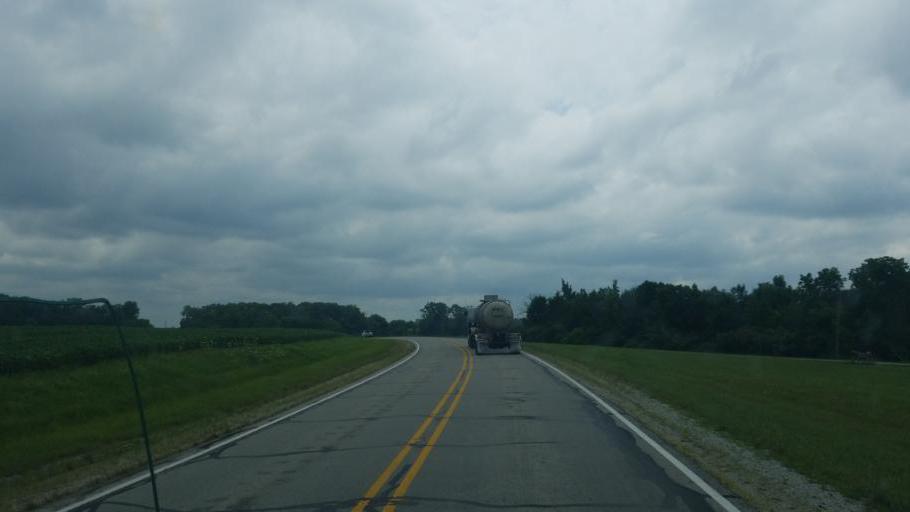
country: US
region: Indiana
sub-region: Huntington County
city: Warren
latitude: 40.6546
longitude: -85.3975
